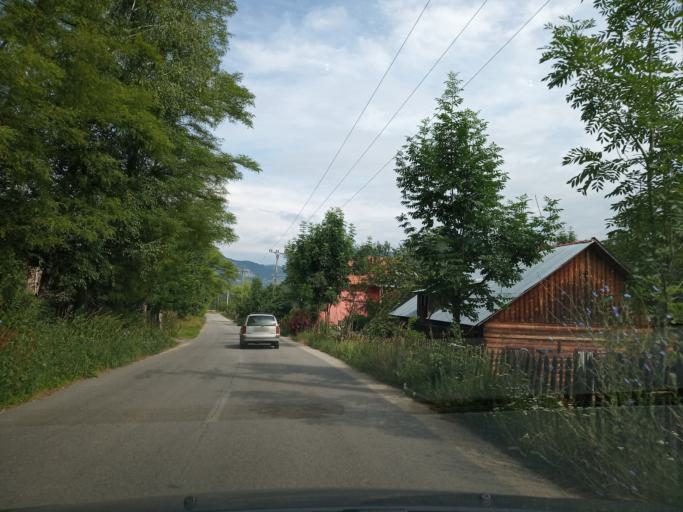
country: RO
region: Hunedoara
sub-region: Oras Petrila
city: Petrila
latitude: 45.4167
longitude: 23.4109
